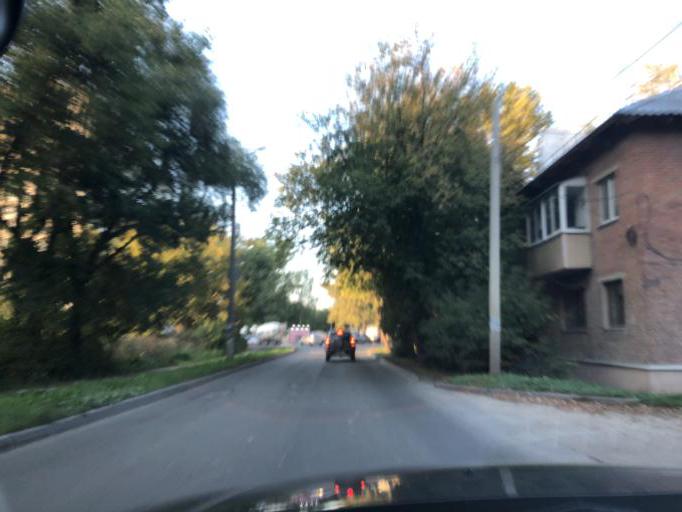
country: RU
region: Tula
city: Tula
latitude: 54.2108
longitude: 37.6292
